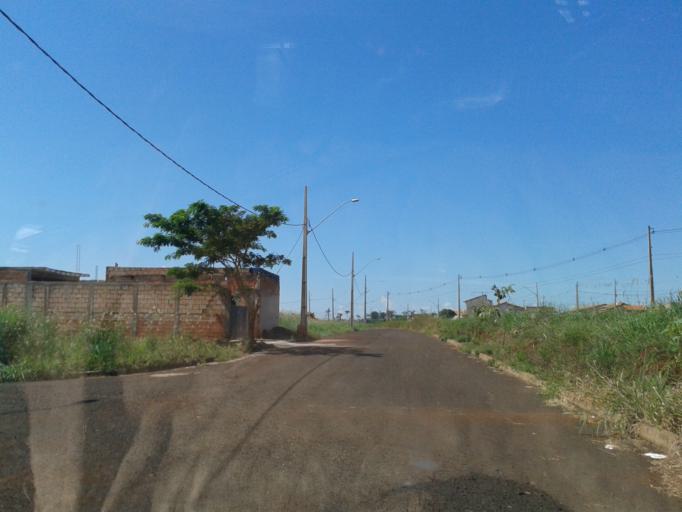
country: BR
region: Goias
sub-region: Itumbiara
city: Itumbiara
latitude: -18.4268
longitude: -49.1856
